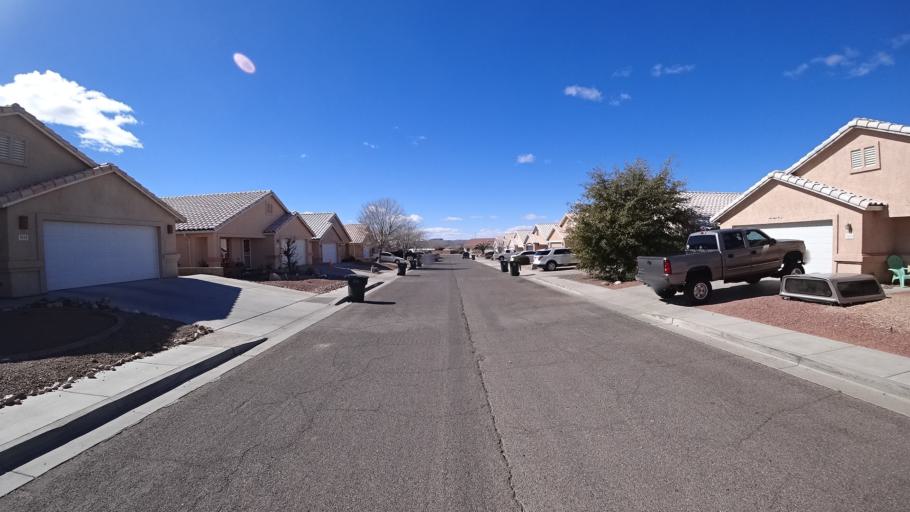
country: US
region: Arizona
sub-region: Mohave County
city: Kingman
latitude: 35.1889
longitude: -114.0079
